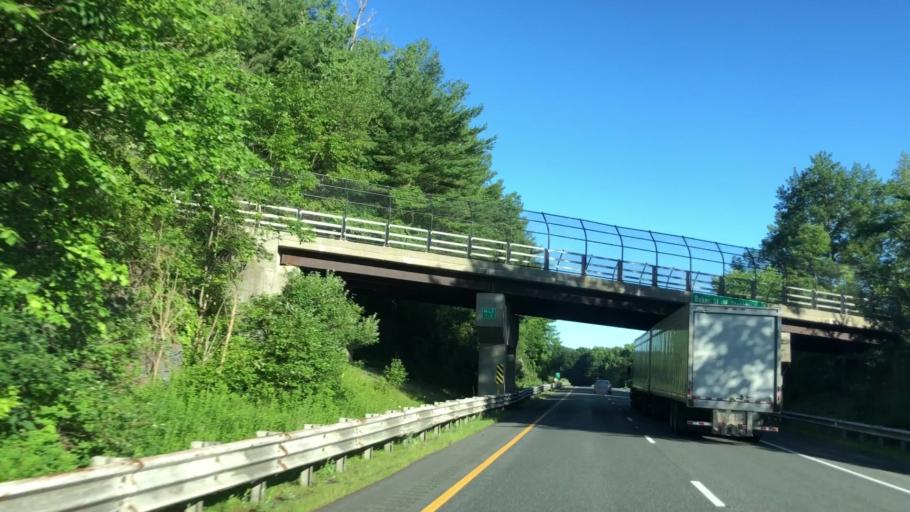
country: US
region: Massachusetts
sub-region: Berkshire County
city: West Stockbridge
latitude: 42.3406
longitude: -73.3899
